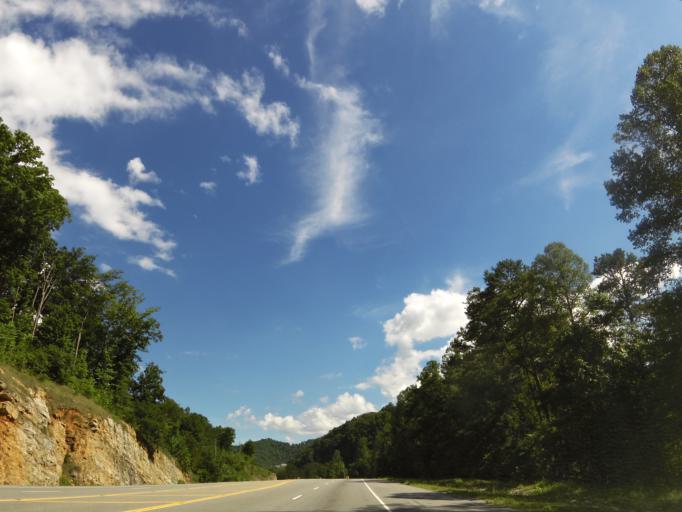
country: US
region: Tennessee
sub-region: Claiborne County
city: Tazewell
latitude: 36.3996
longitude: -83.4569
